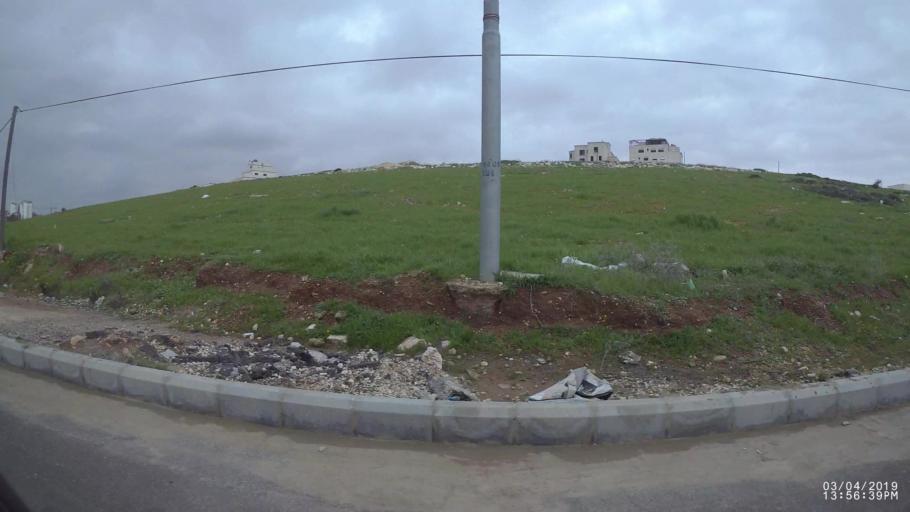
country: JO
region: Amman
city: Wadi as Sir
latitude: 31.9326
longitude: 35.8478
